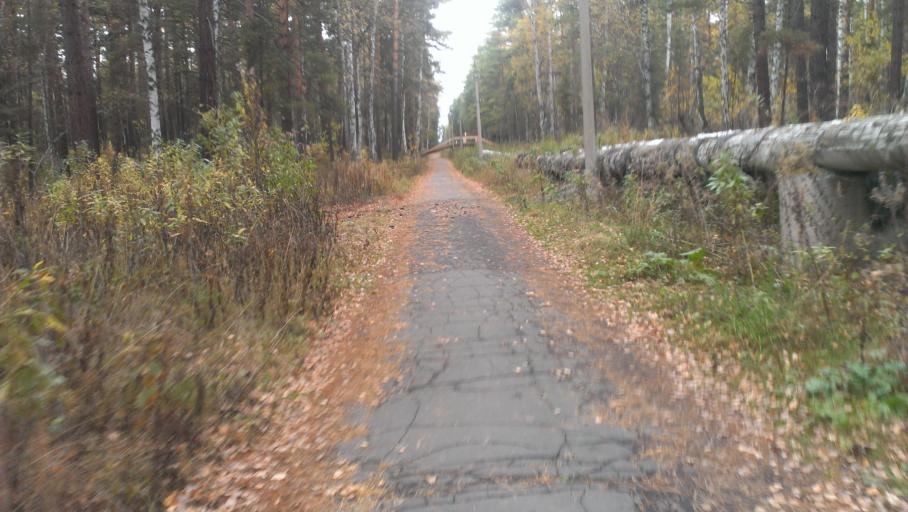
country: RU
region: Altai Krai
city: Yuzhnyy
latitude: 53.2637
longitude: 83.6859
